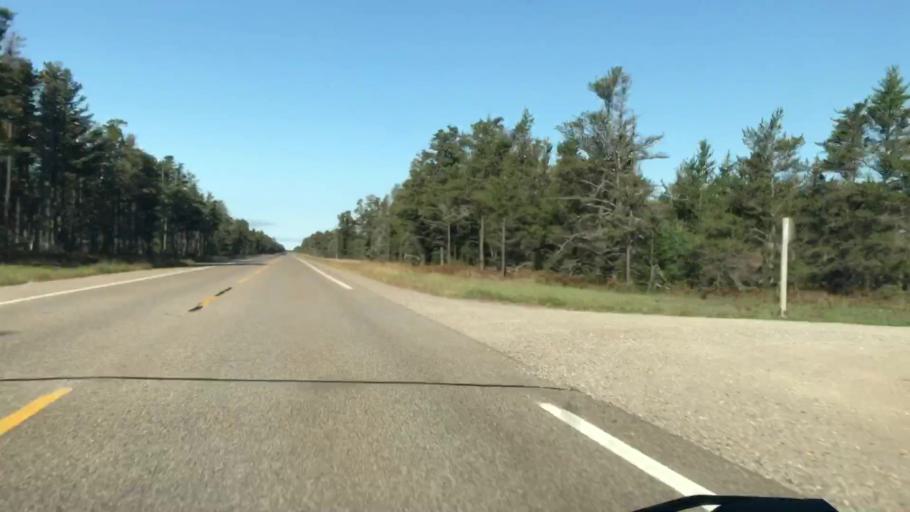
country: US
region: Michigan
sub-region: Mackinac County
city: Saint Ignace
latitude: 46.3587
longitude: -84.8298
